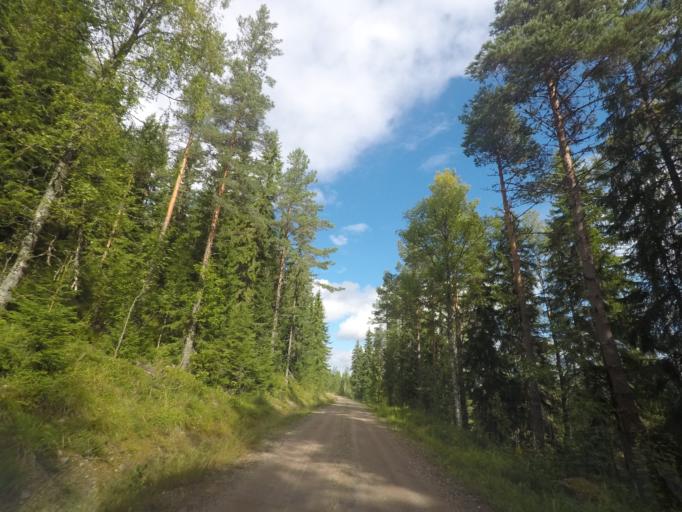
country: SE
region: Vaermland
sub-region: Filipstads Kommun
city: Lesjofors
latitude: 60.0466
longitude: 14.4434
